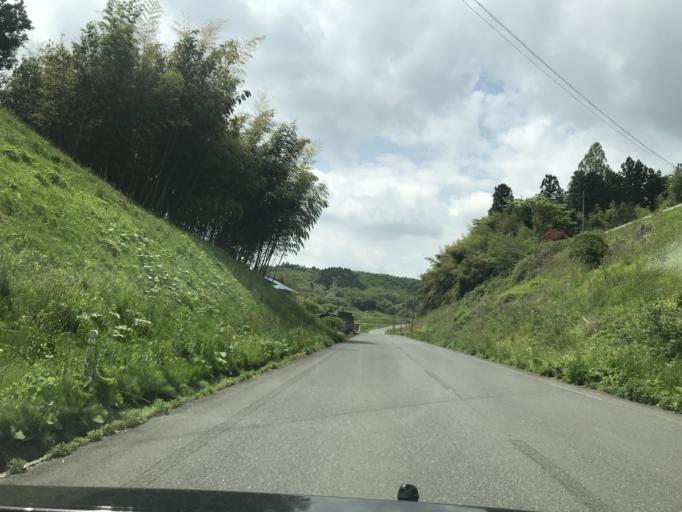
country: JP
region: Miyagi
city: Furukawa
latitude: 38.7268
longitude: 140.9261
